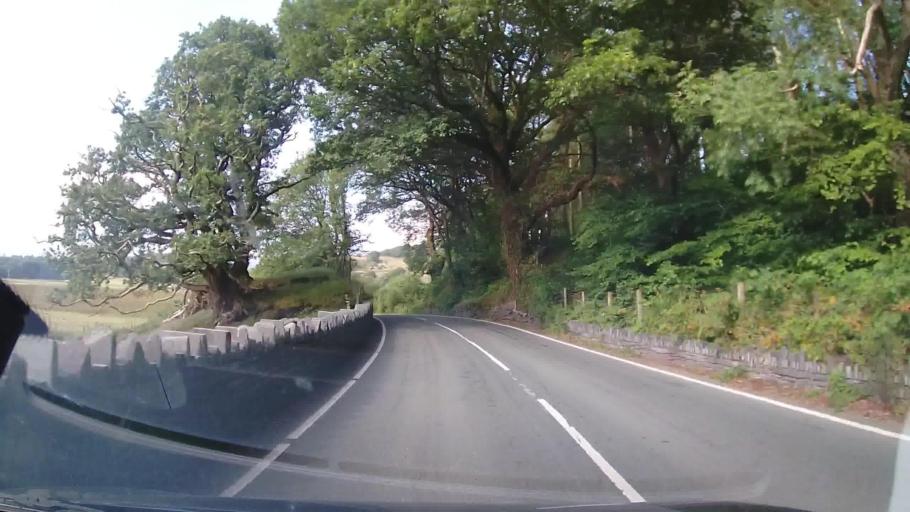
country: GB
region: Wales
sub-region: Gwynedd
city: Penrhyndeudraeth
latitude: 52.9106
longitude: -4.0537
